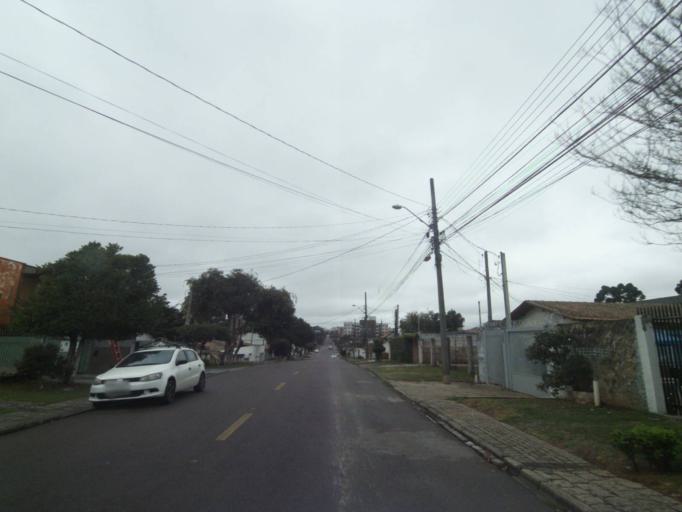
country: BR
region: Parana
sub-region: Curitiba
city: Curitiba
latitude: -25.5153
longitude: -49.3036
